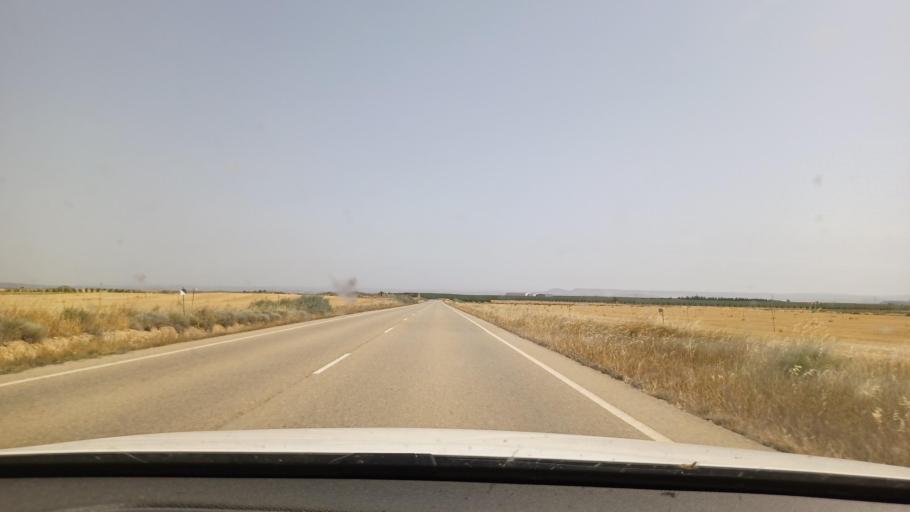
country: ES
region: Aragon
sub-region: Provincia de Zaragoza
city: Chiprana
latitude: 41.3147
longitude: -0.0760
